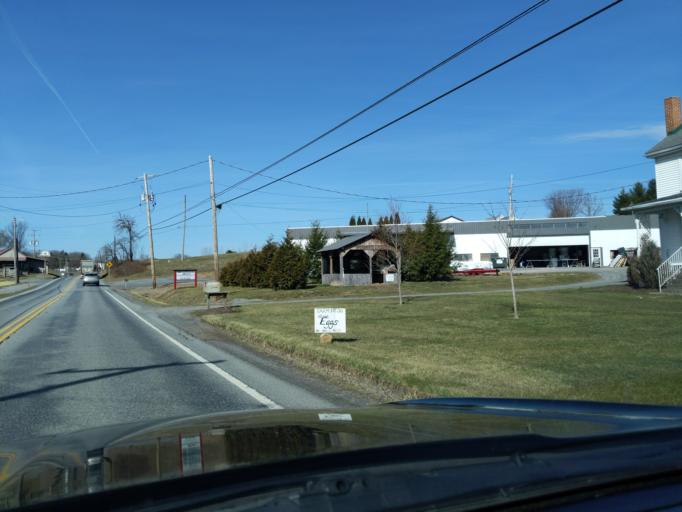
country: US
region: Pennsylvania
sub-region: Blair County
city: Martinsburg
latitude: 40.3092
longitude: -78.3099
